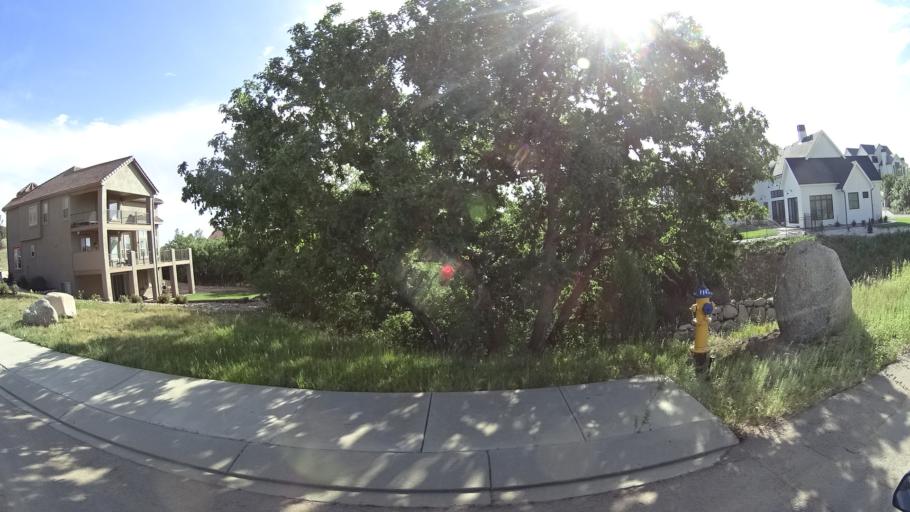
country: US
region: Colorado
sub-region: El Paso County
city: Fort Carson
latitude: 38.7530
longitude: -104.8182
